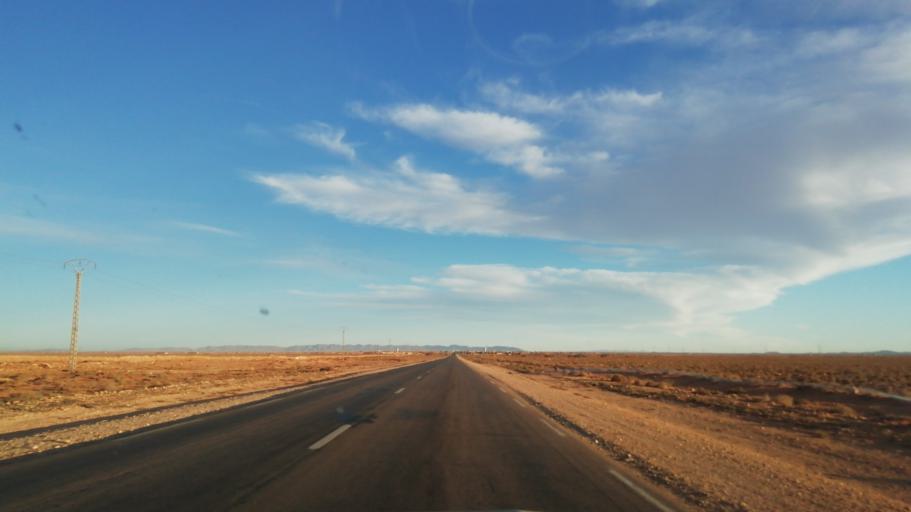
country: DZ
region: Wilaya de Naama
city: Naama
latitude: 33.7328
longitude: -0.7569
